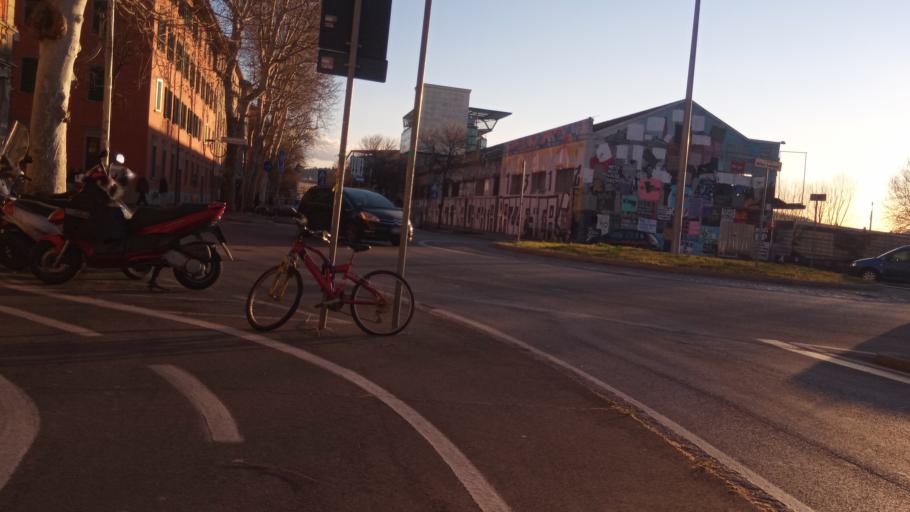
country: IT
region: Emilia-Romagna
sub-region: Provincia di Bologna
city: Bologna
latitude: 44.5131
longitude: 11.3416
